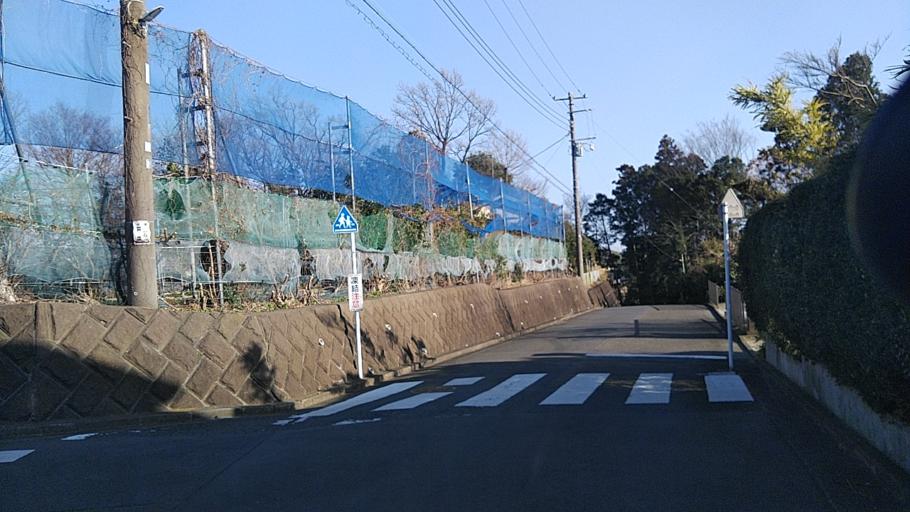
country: JP
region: Kanagawa
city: Fujisawa
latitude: 35.4074
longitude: 139.4729
